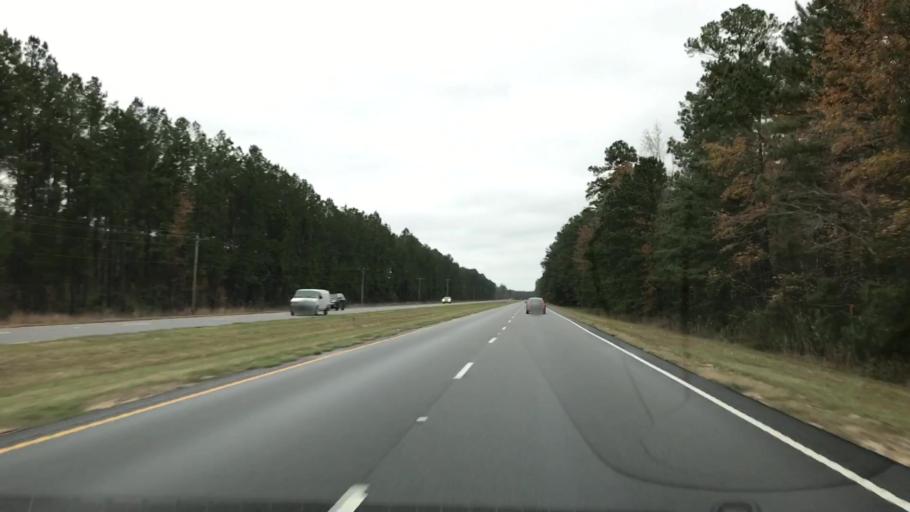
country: US
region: South Carolina
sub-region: Georgetown County
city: Georgetown
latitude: 33.2805
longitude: -79.3506
